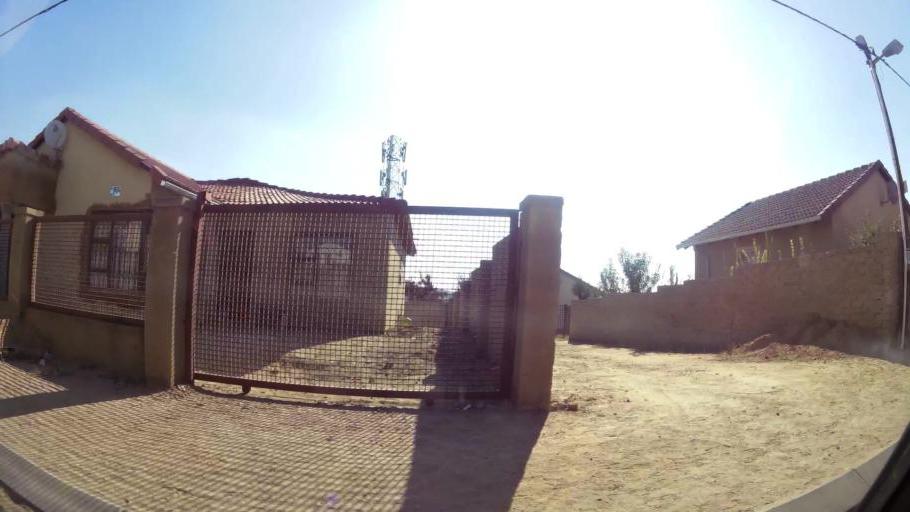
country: ZA
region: Gauteng
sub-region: West Rand District Municipality
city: Muldersdriseloop
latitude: -26.0380
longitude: 27.9241
